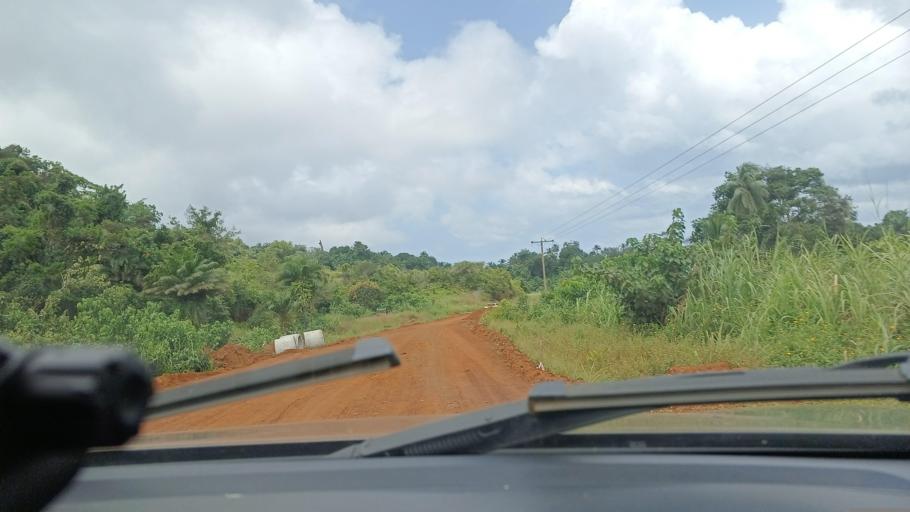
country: LR
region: Grand Cape Mount
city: Robertsport
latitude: 6.7500
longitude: -11.3608
